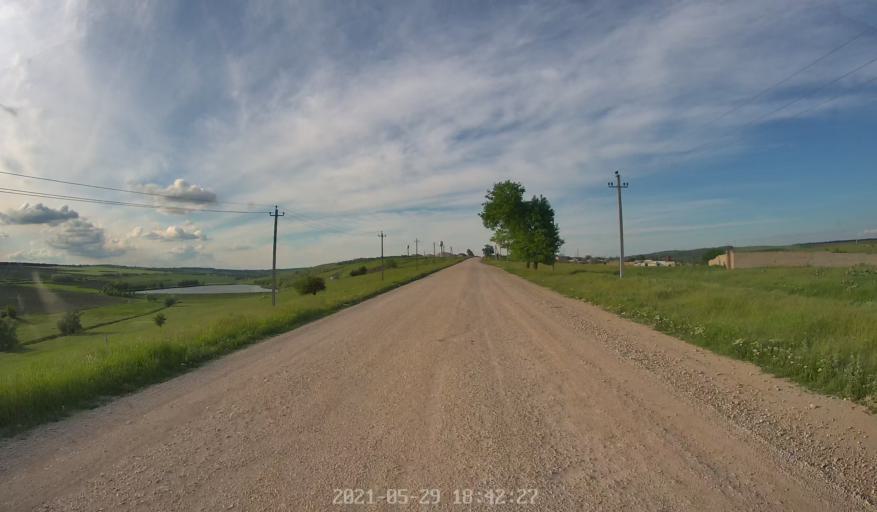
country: MD
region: Chisinau
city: Singera
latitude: 46.8122
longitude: 28.9620
